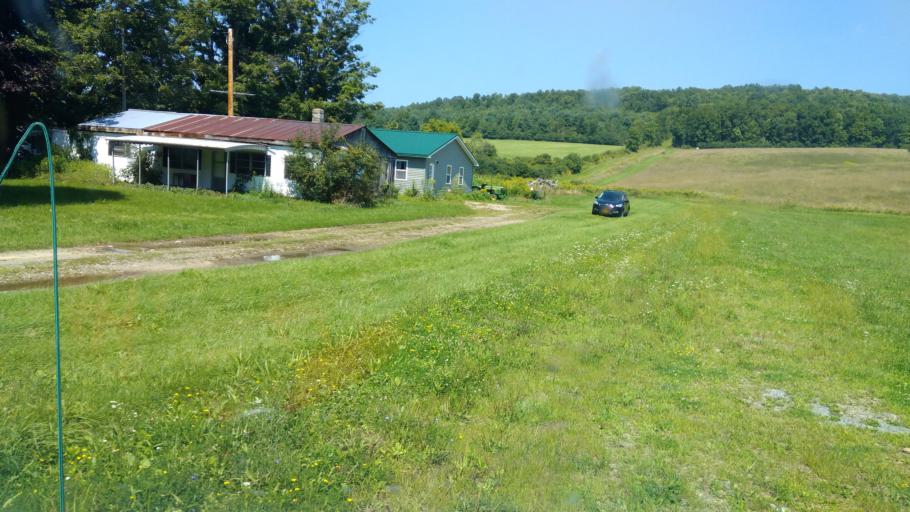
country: US
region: New York
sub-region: Allegany County
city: Belmont
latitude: 42.3021
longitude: -78.0002
